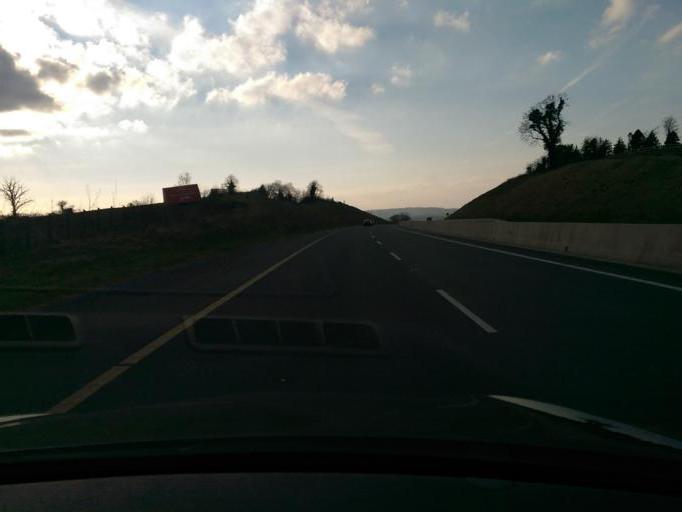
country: IE
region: Munster
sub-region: North Tipperary
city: Roscrea
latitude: 52.9152
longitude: -7.7099
